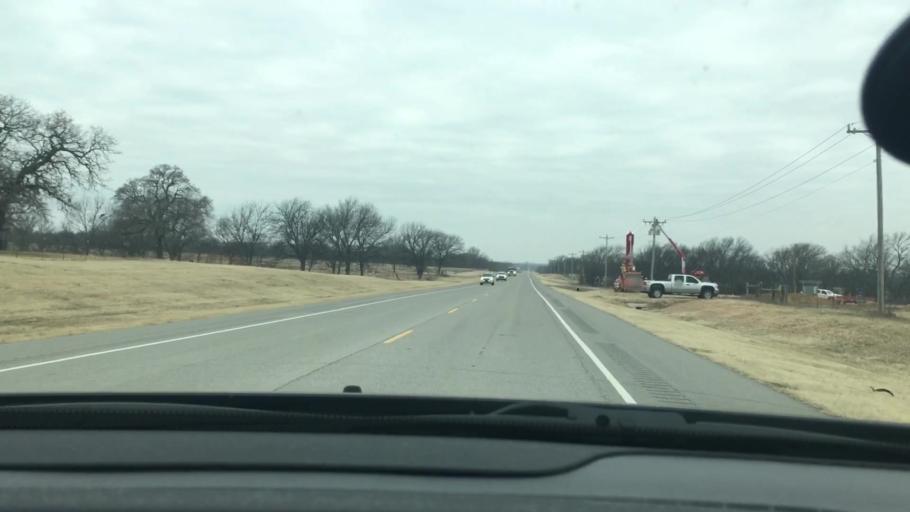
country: US
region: Oklahoma
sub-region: Carter County
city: Healdton
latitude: 34.4924
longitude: -97.4195
